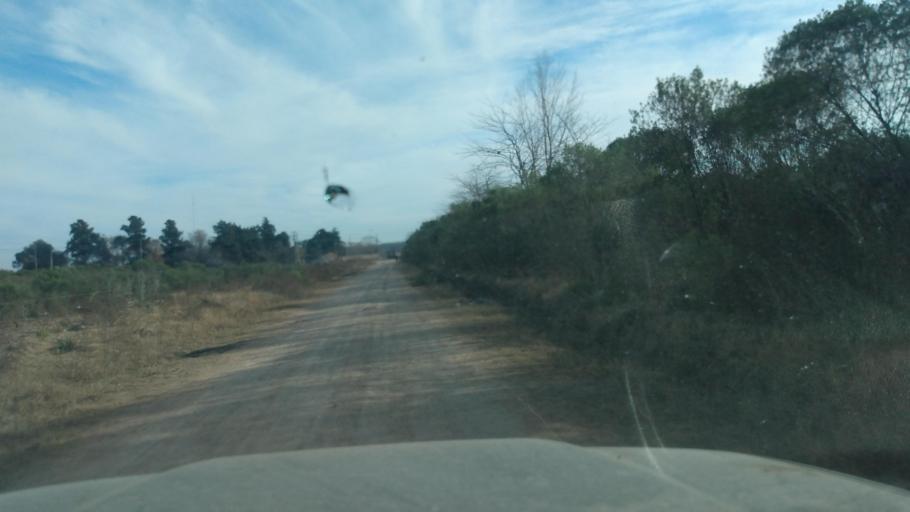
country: AR
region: Buenos Aires
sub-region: Partido de Lujan
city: Lujan
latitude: -34.5348
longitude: -59.1156
